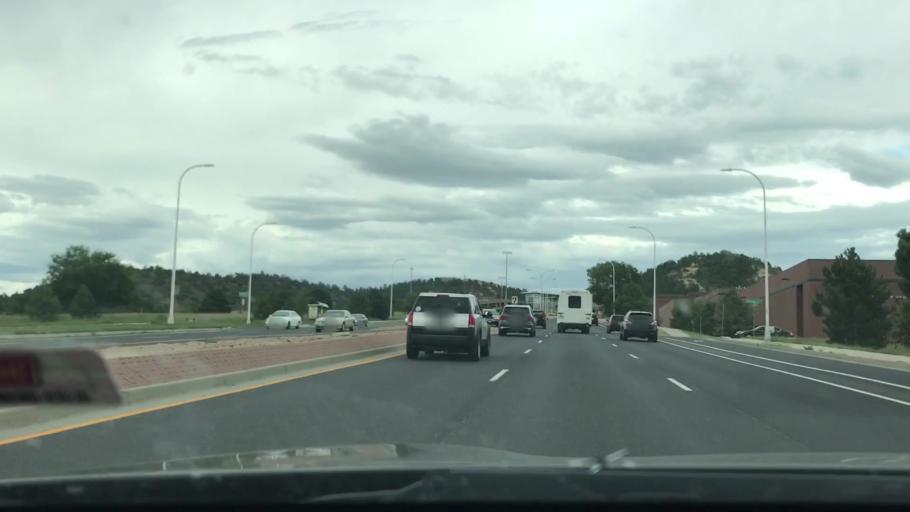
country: US
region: Colorado
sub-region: El Paso County
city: Colorado Springs
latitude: 38.8977
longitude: -104.8134
